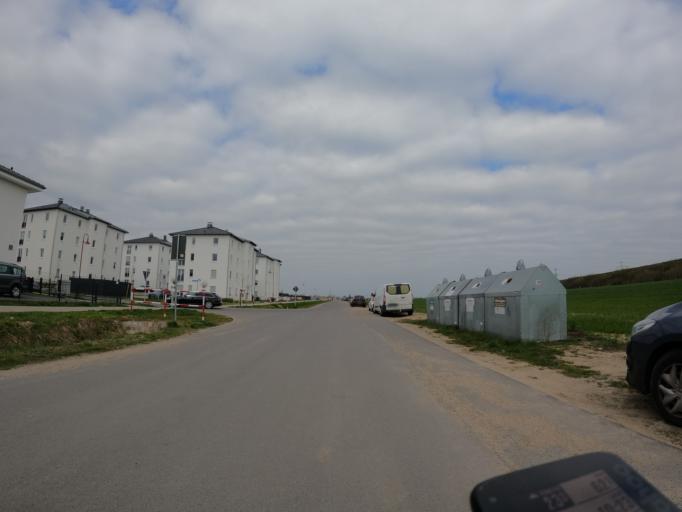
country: DE
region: Brandenburg
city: Neuenhagen
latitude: 52.5293
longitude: 13.7080
